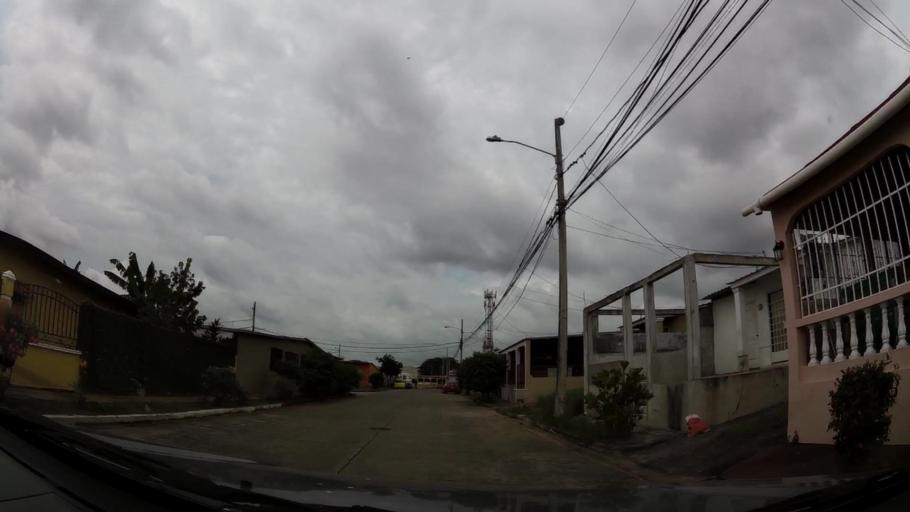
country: PA
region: Panama
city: San Miguelito
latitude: 9.0589
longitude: -79.4237
